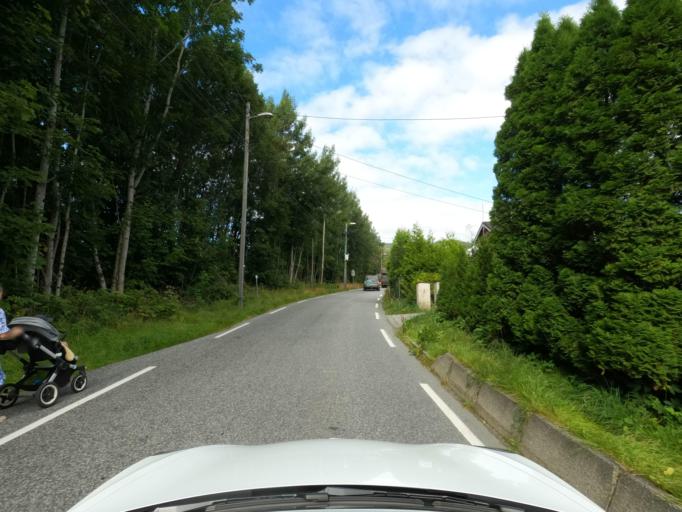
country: NO
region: Hordaland
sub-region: Bergen
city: Sandsli
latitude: 60.2649
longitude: 5.3513
